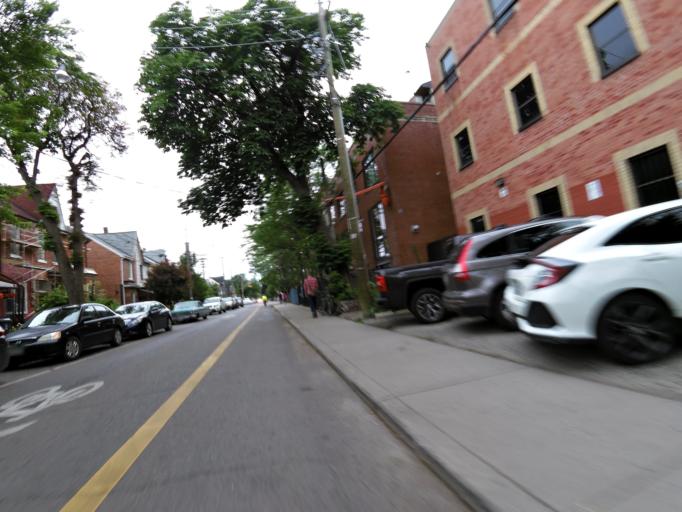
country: CA
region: Ontario
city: Toronto
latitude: 43.6462
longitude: -79.4052
